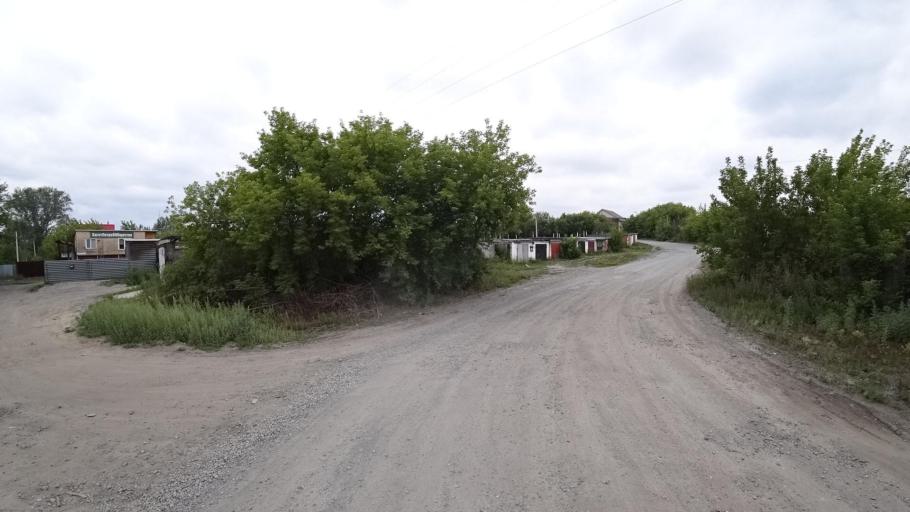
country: RU
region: Sverdlovsk
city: Kamyshlov
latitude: 56.8340
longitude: 62.7188
